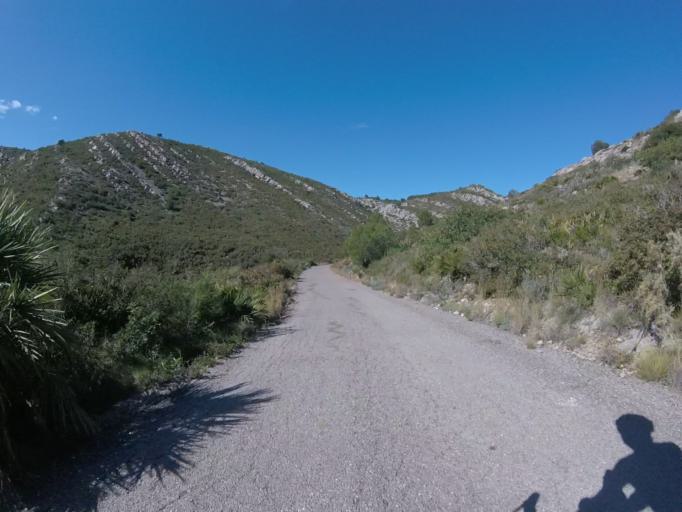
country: ES
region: Valencia
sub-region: Provincia de Castello
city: Benicassim
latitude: 40.0770
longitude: 0.1069
